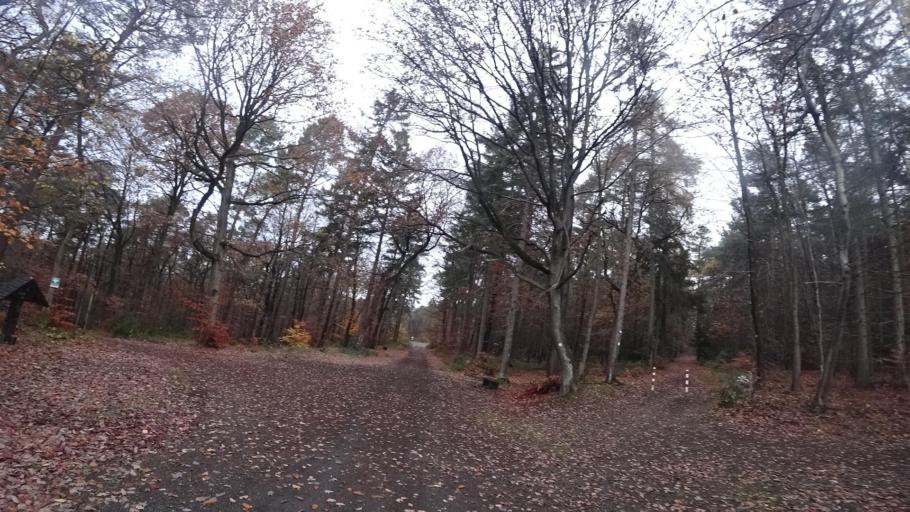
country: DE
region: Rheinland-Pfalz
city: Schalkenbach
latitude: 50.5154
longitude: 7.1297
